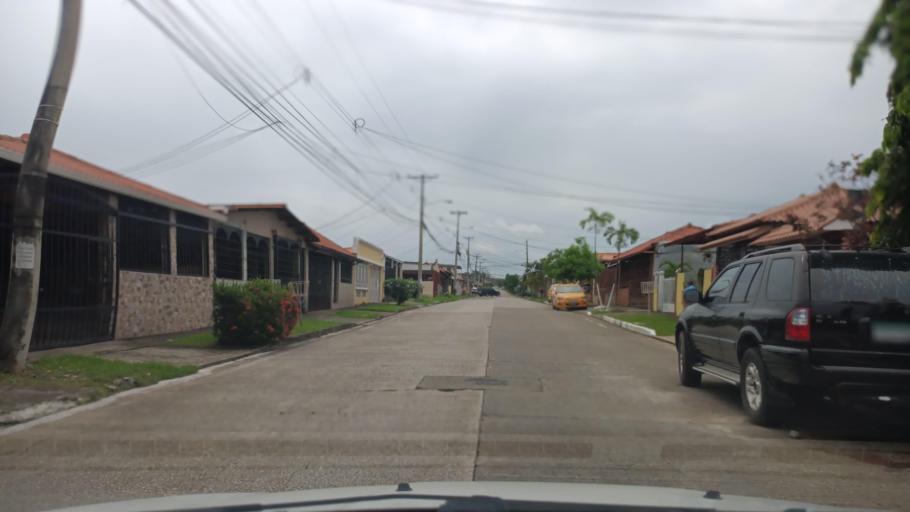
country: PA
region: Panama
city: Tocumen
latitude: 9.0505
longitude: -79.4181
